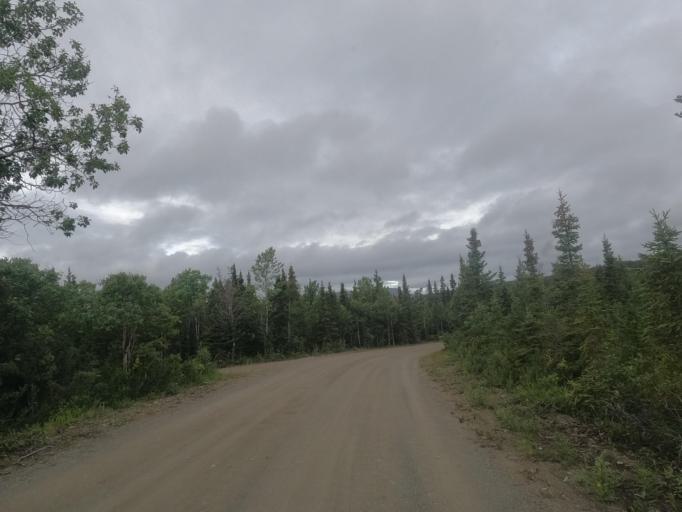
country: CA
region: Yukon
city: Haines Junction
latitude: 60.1084
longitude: -136.9369
